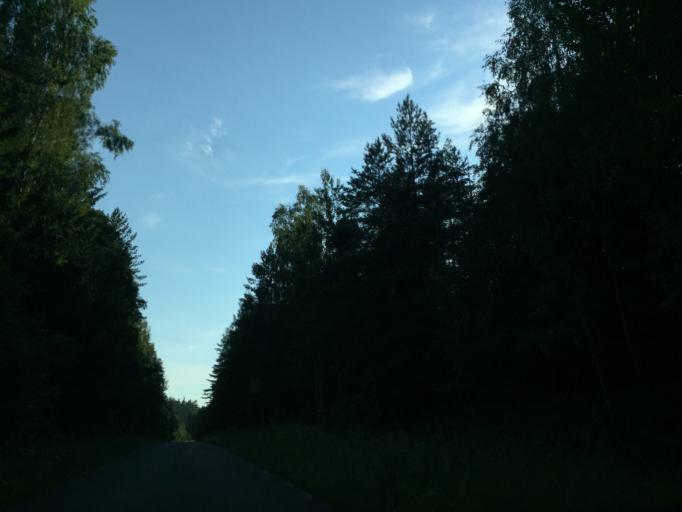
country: LV
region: Krimulda
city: Ragana
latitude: 57.1346
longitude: 24.7632
